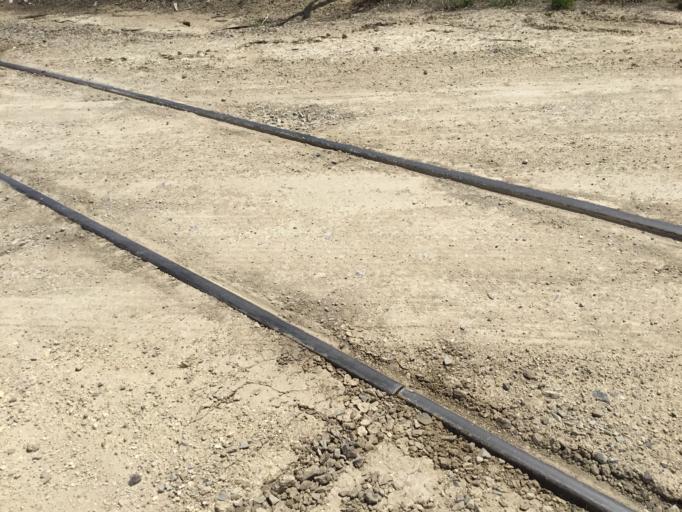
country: US
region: Kansas
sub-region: Mitchell County
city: Beloit
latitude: 39.5298
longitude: -98.0043
